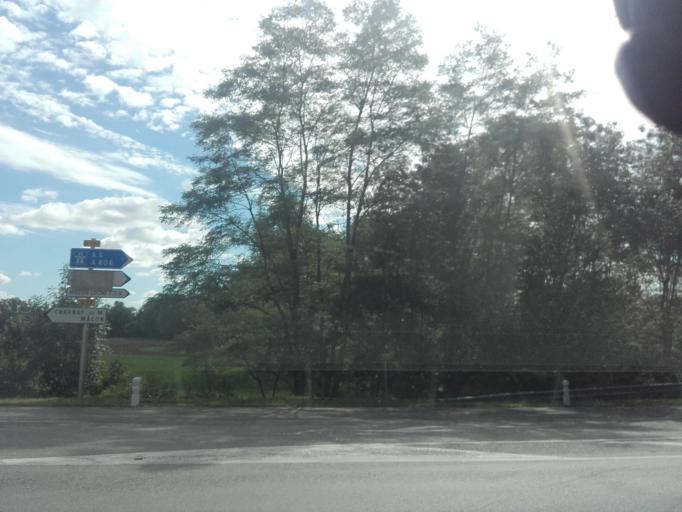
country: FR
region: Bourgogne
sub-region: Departement de Saone-et-Loire
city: Prisse
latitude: 46.3329
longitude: 4.7364
